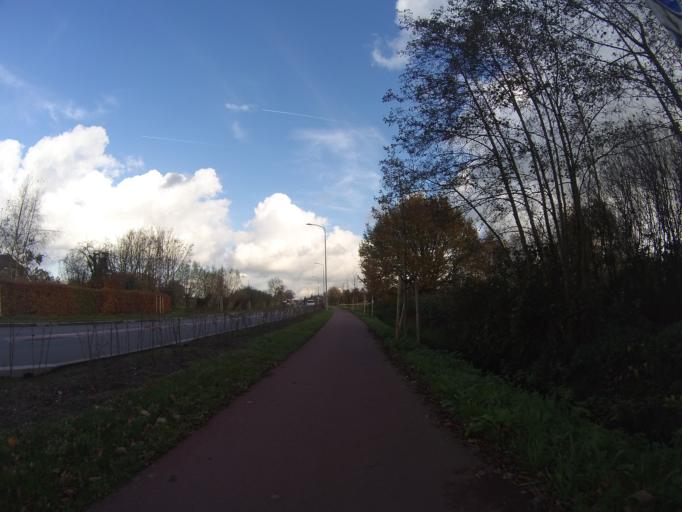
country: NL
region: Gelderland
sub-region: Gemeente Nijkerk
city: Nijkerk
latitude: 52.1947
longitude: 5.4502
